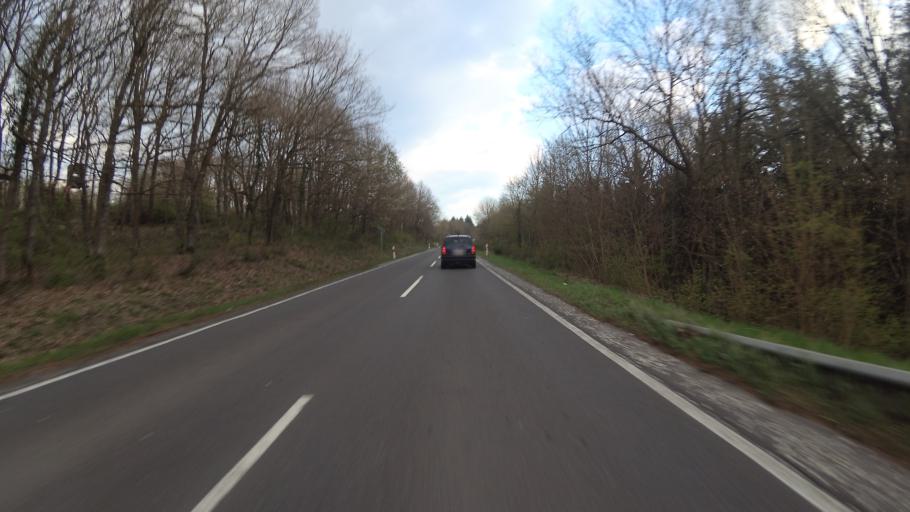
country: DE
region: Rheinland-Pfalz
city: Veldenz
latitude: 49.8991
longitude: 7.0297
